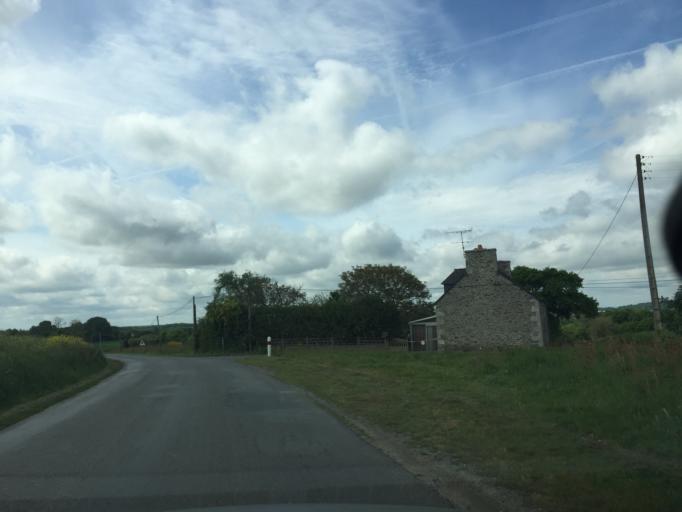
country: FR
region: Brittany
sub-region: Departement des Cotes-d'Armor
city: Crehen
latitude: 48.5364
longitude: -2.1875
